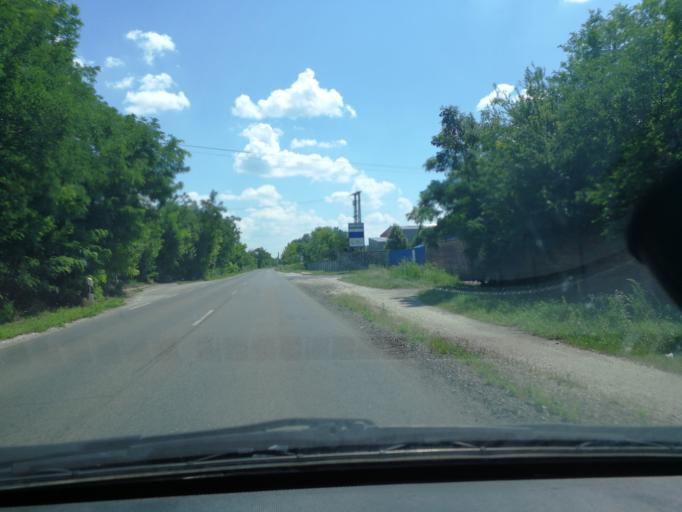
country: HU
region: Pest
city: Halasztelek
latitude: 47.3473
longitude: 18.9907
